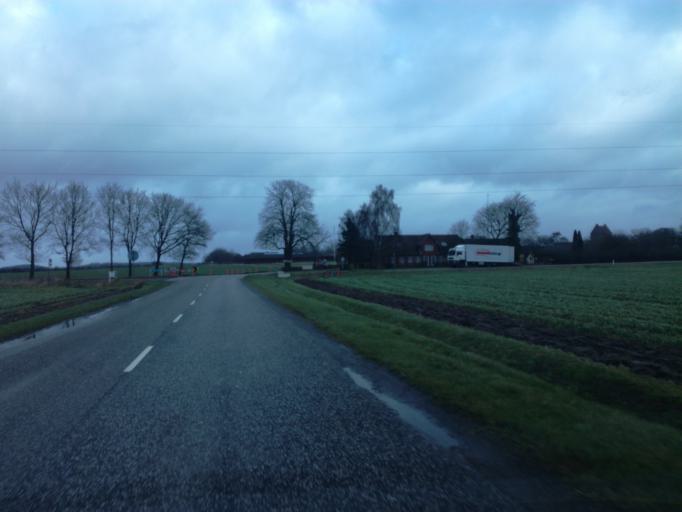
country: DK
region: South Denmark
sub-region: Vejle Kommune
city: Brejning
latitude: 55.6350
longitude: 9.6878
